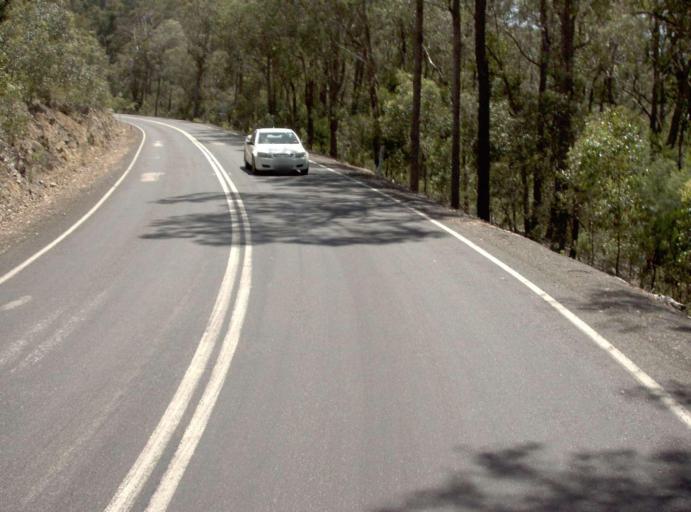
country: AU
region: Victoria
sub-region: East Gippsland
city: Lakes Entrance
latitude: -37.6213
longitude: 147.8830
